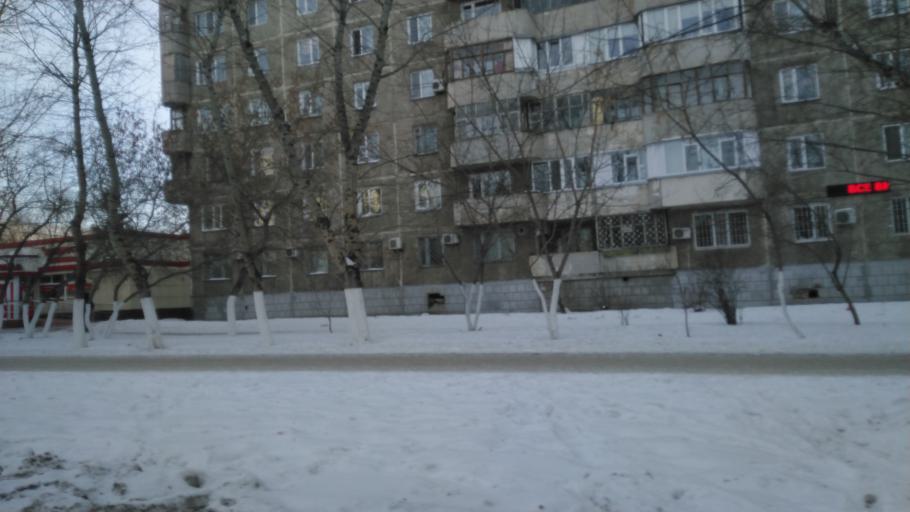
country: KZ
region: Pavlodar
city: Pavlodar
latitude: 52.2674
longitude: 76.9464
